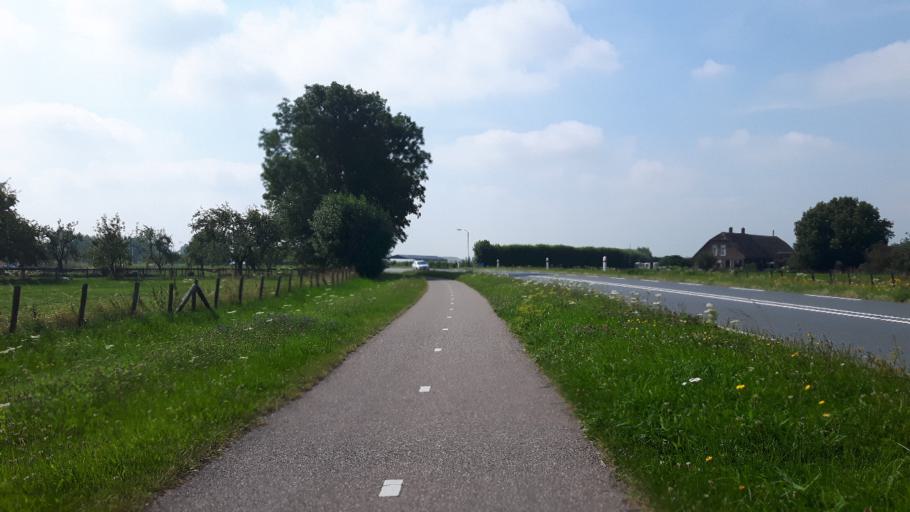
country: NL
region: Utrecht
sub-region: Gemeente Montfoort
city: Montfoort
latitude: 52.0492
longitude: 4.9278
